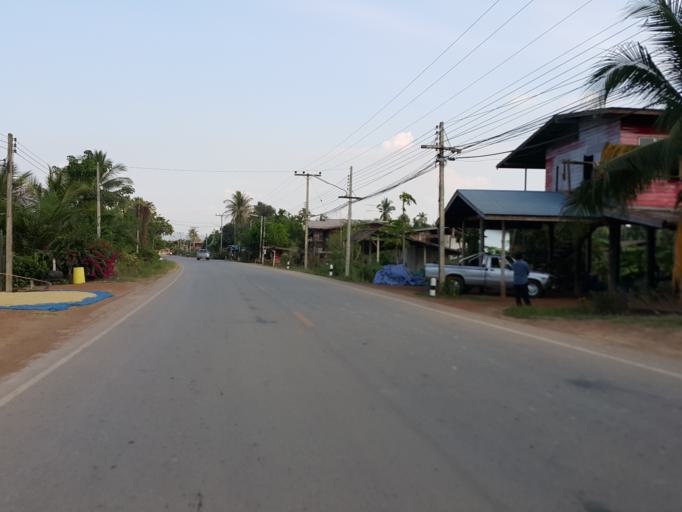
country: TH
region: Sukhothai
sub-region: Amphoe Si Satchanalai
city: Si Satchanalai
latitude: 17.4295
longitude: 99.6940
